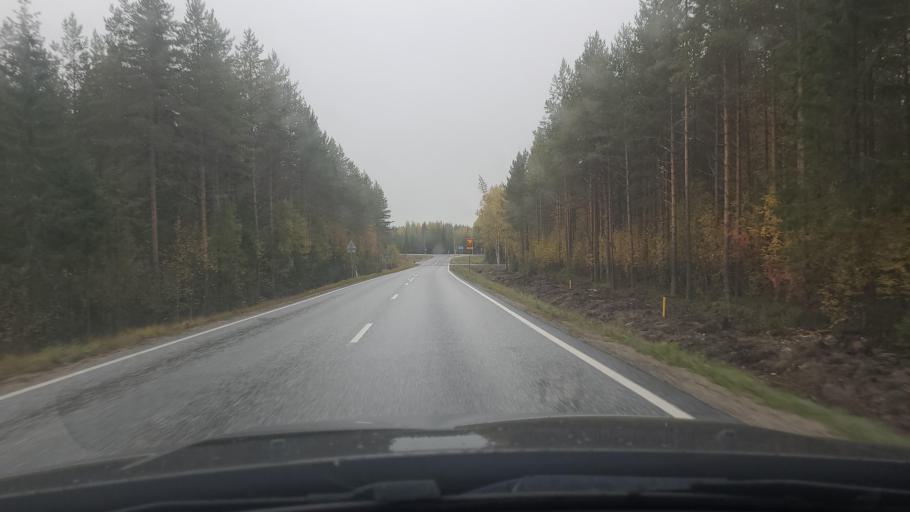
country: FI
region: Northern Savo
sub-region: Varkaus
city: Kangaslampi
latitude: 62.4599
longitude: 28.3222
